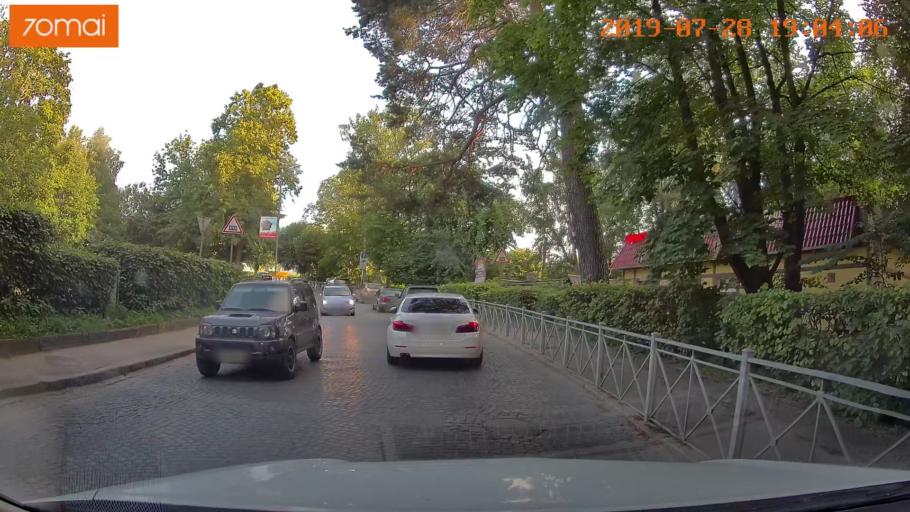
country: RU
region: Kaliningrad
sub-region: Gorod Svetlogorsk
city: Svetlogorsk
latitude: 54.9344
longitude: 20.1613
